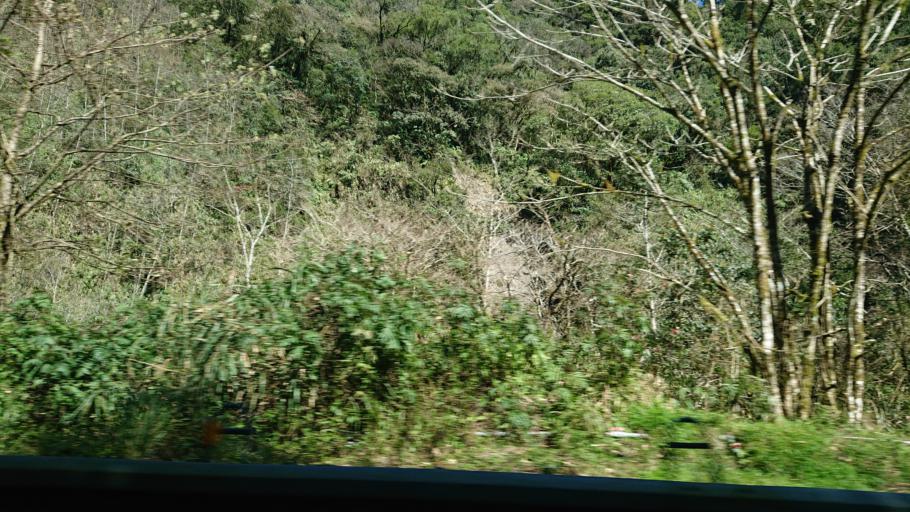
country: TW
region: Taiwan
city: Daxi
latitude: 24.4124
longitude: 121.3585
